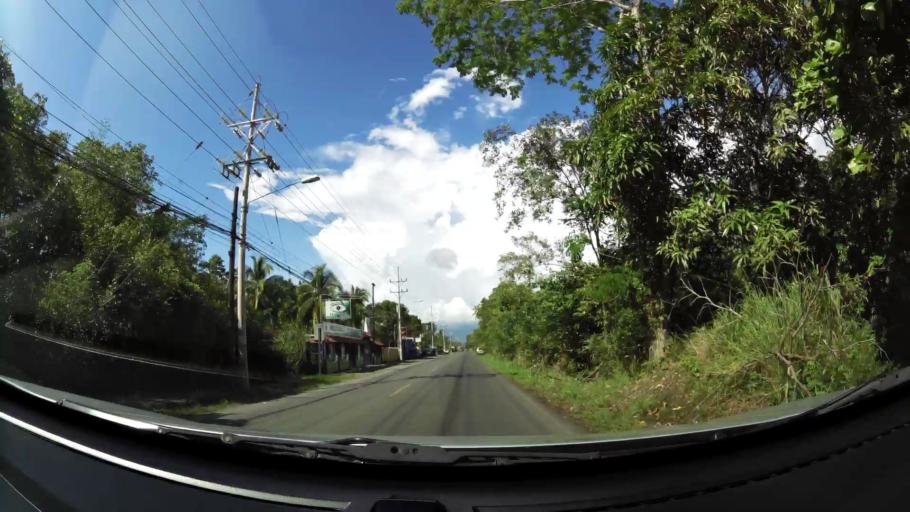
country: CR
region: Puntarenas
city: Quepos
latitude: 9.4392
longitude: -84.1646
